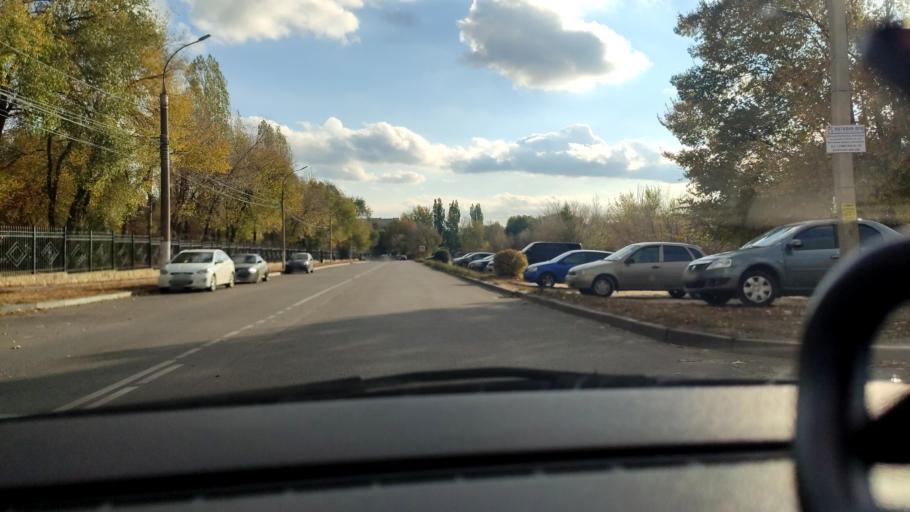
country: RU
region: Voronezj
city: Pridonskoy
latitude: 51.6511
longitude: 39.1006
